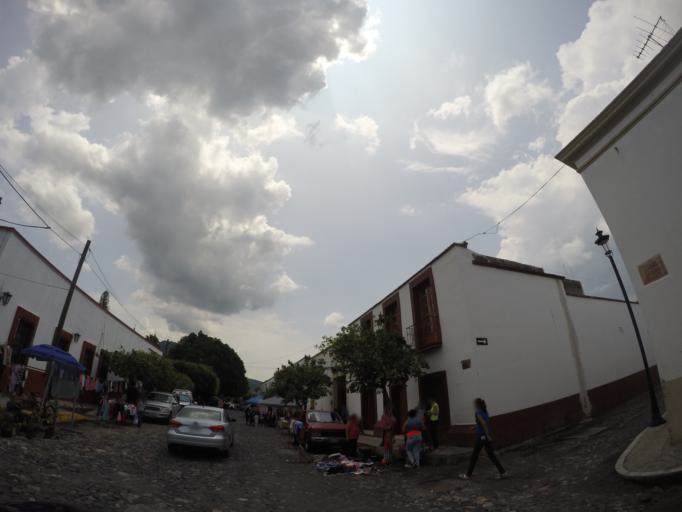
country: MX
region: Nayarit
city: Jala
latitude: 21.1068
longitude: -104.4432
